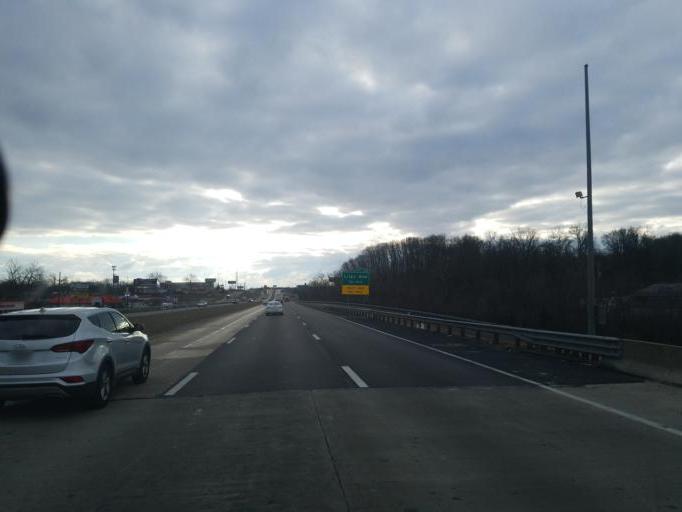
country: US
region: Missouri
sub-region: Saint Louis County
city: Spanish Lake
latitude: 38.7699
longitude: -90.2209
